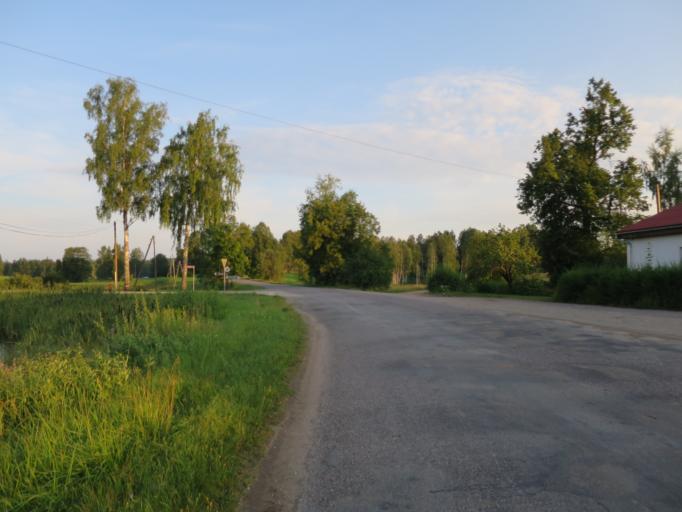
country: LV
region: Amatas Novads
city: Drabesi
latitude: 57.2535
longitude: 25.2776
